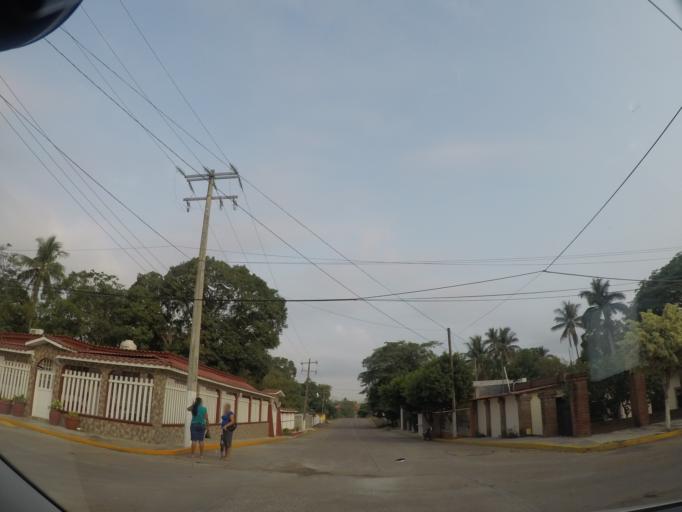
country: MX
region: Oaxaca
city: Matias Romero
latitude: 16.8715
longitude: -95.0422
